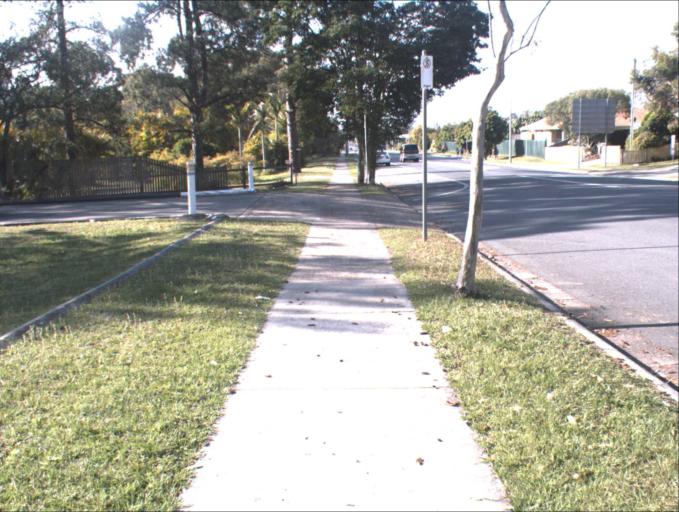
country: AU
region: Queensland
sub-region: Logan
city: Logan Reserve
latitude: -27.6800
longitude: 153.0888
